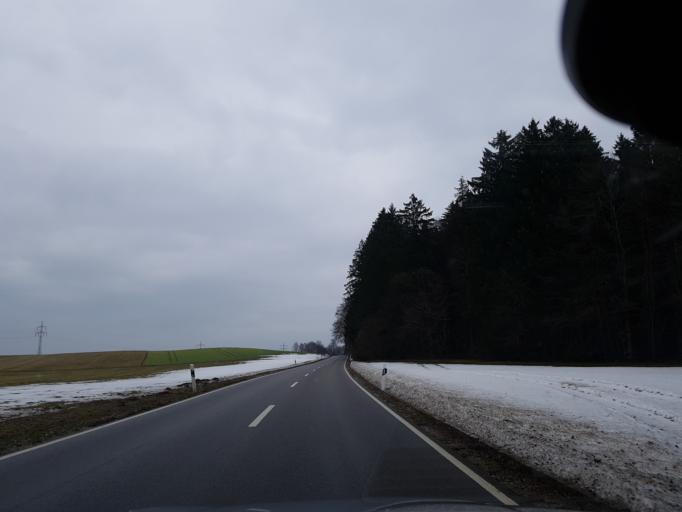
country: DE
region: Bavaria
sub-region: Upper Bavaria
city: Feldkirchen-Westerham
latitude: 47.9398
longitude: 11.8315
